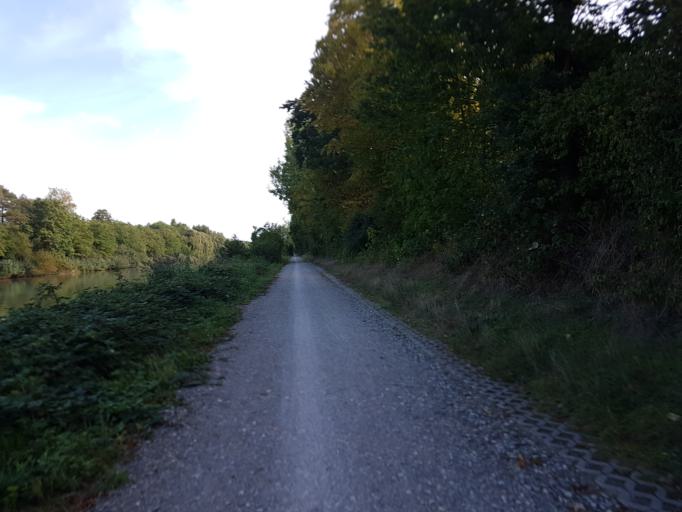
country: DE
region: Lower Saxony
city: Isernhagen Farster Bauerschaft
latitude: 52.3953
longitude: 9.8257
